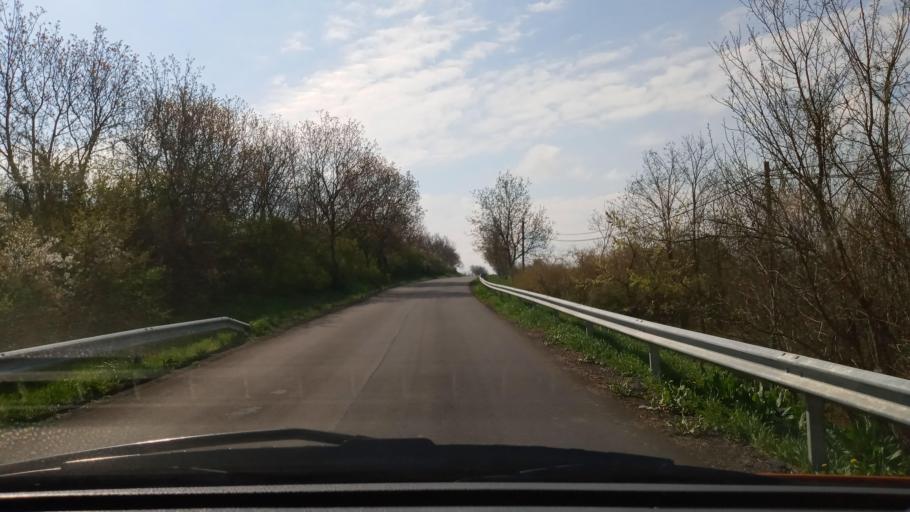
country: HU
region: Baranya
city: Pecsvarad
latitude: 46.0997
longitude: 18.4620
